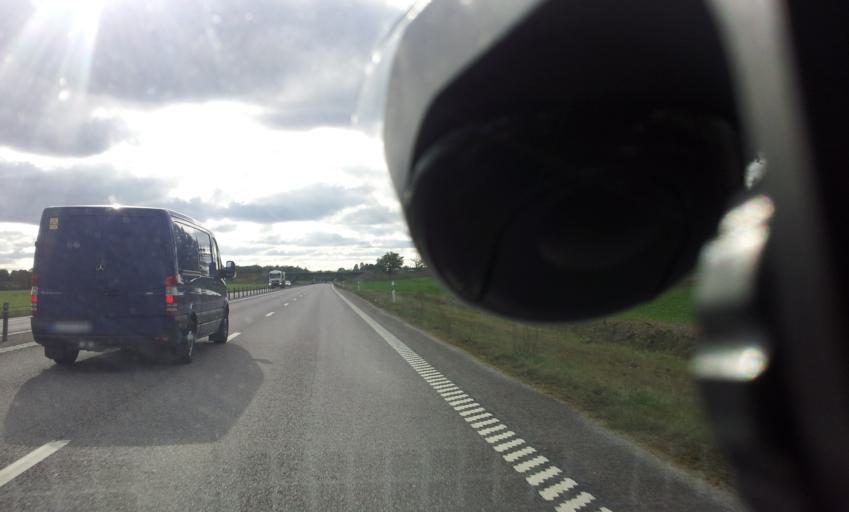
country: SE
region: Kalmar
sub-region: Kalmar Kommun
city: Ljungbyholm
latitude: 56.5774
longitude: 16.1103
